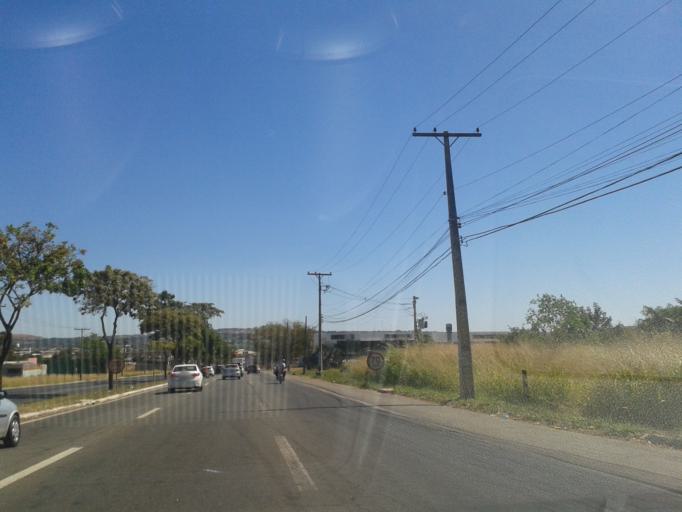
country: BR
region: Goias
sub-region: Goiania
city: Goiania
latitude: -16.6436
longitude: -49.2963
